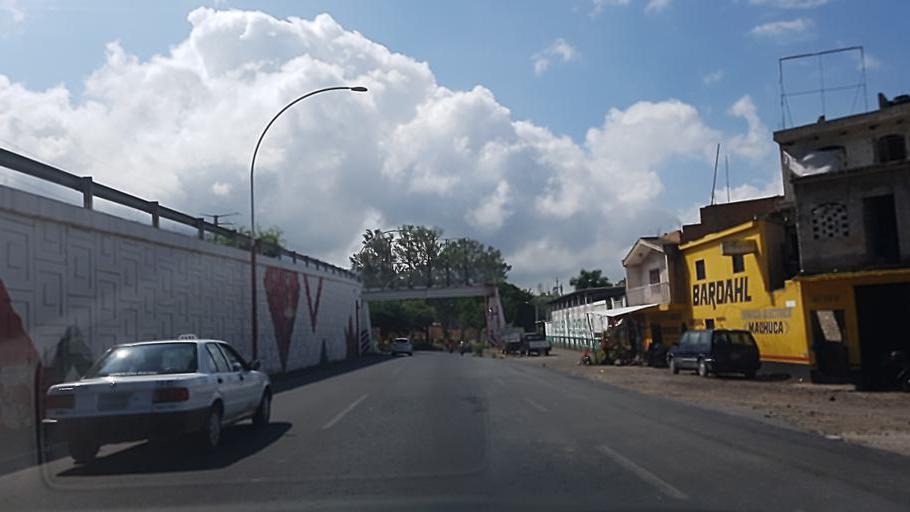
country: MX
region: Nayarit
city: Tepic
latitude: 21.4856
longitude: -104.9023
